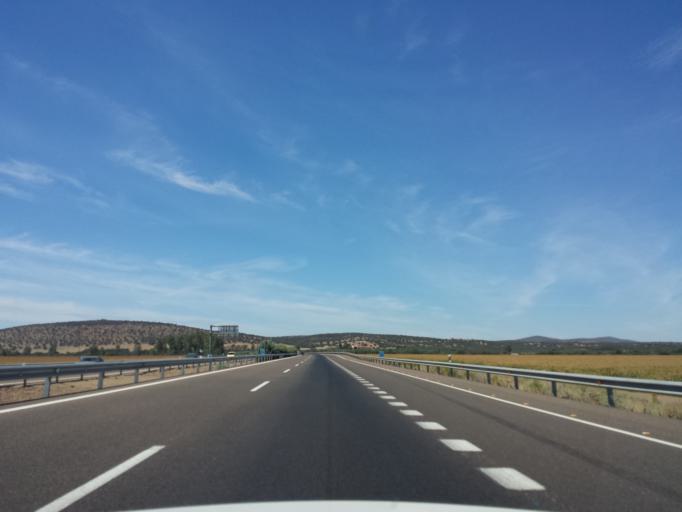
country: ES
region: Extremadura
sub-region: Provincia de Badajoz
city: San Pedro de Merida
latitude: 38.9896
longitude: -6.1256
